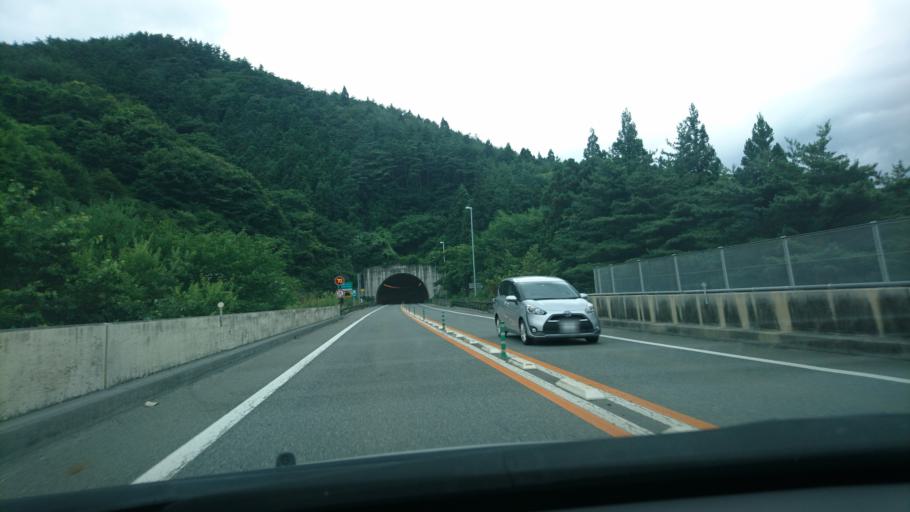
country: JP
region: Iwate
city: Ofunato
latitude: 39.0603
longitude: 141.7099
